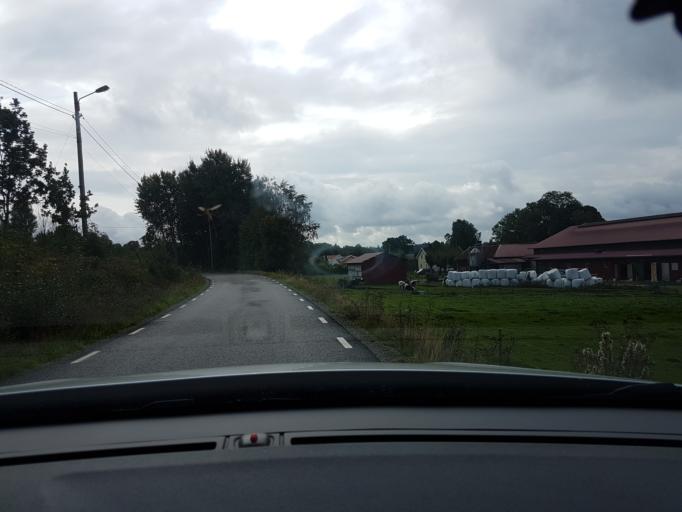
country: SE
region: Vaestra Goetaland
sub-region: Ale Kommun
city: Skepplanda
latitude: 57.8952
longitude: 12.1938
